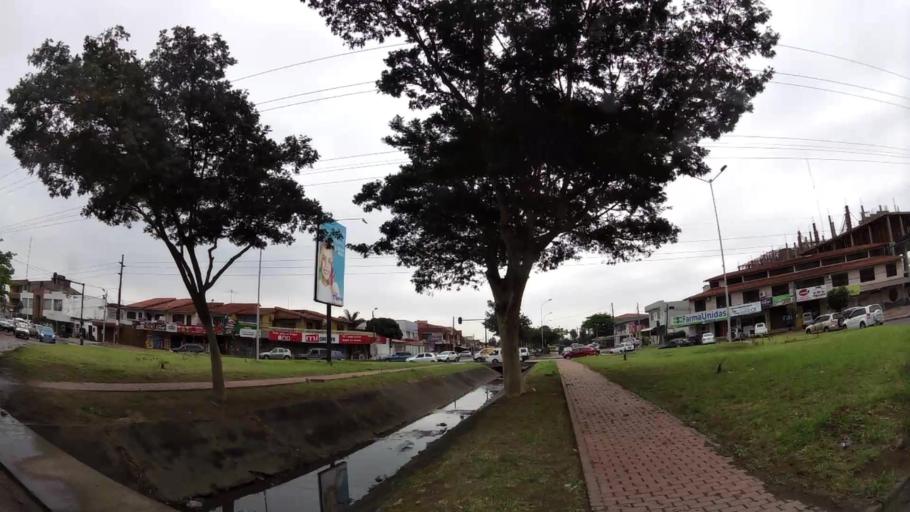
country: BO
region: Santa Cruz
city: Santa Cruz de la Sierra
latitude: -17.7611
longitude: -63.1675
